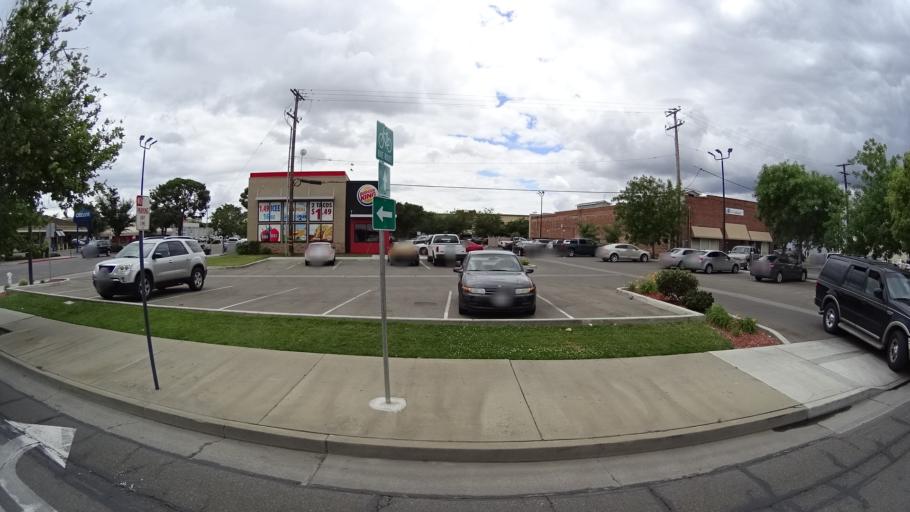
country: US
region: California
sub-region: Kings County
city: Hanford
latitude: 36.3279
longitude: -119.6497
